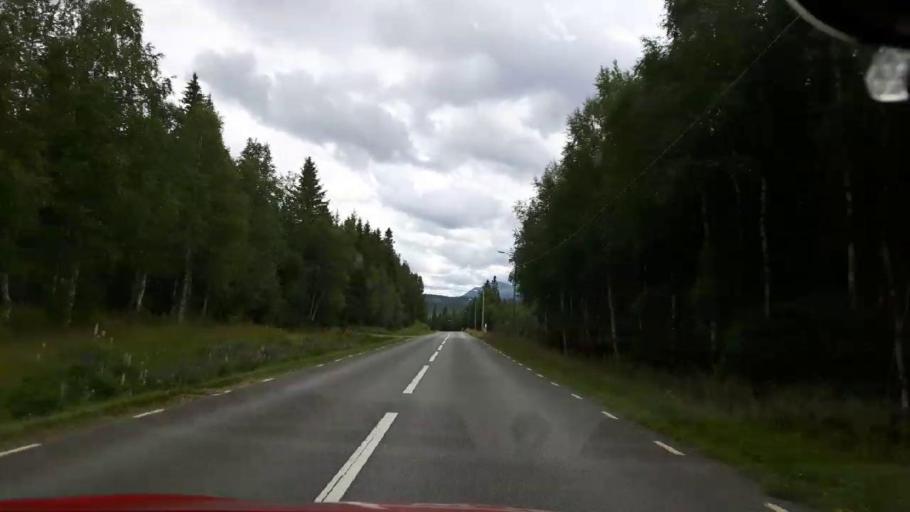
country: NO
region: Nord-Trondelag
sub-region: Lierne
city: Sandvika
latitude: 64.3929
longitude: 14.3693
